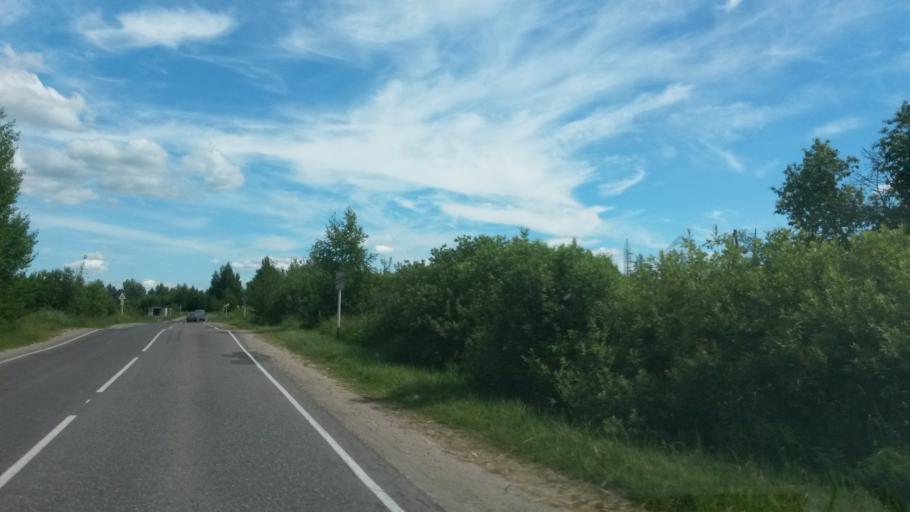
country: RU
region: Ivanovo
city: Zavolzhsk
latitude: 57.5030
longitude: 42.1106
